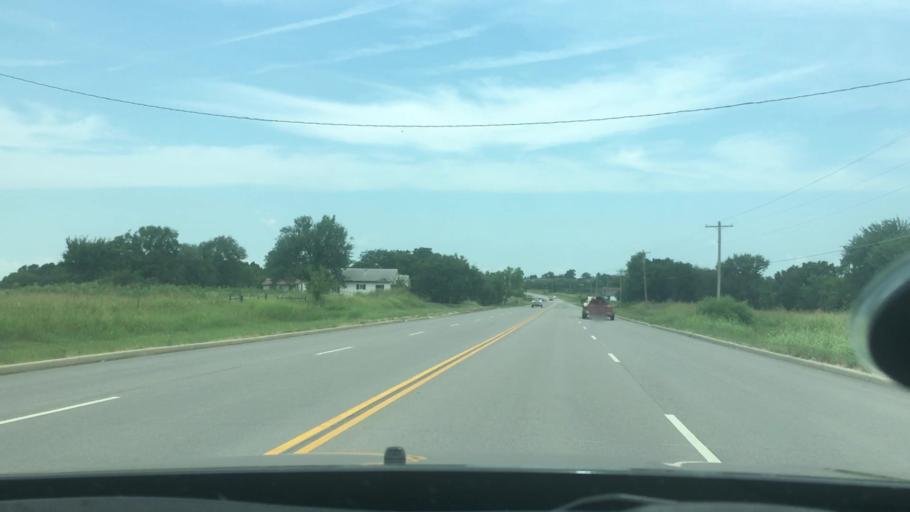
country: US
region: Oklahoma
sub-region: Seminole County
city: Seminole
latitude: 35.2663
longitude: -96.7168
